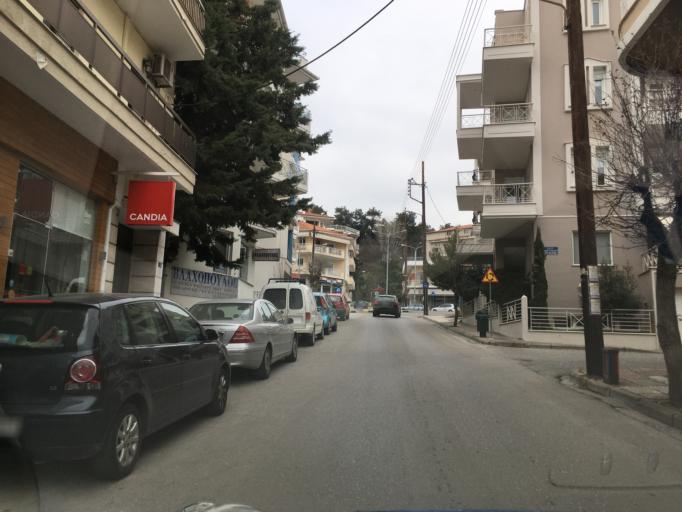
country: GR
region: West Macedonia
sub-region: Nomos Kozanis
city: Kozani
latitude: 40.3013
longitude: 21.7950
